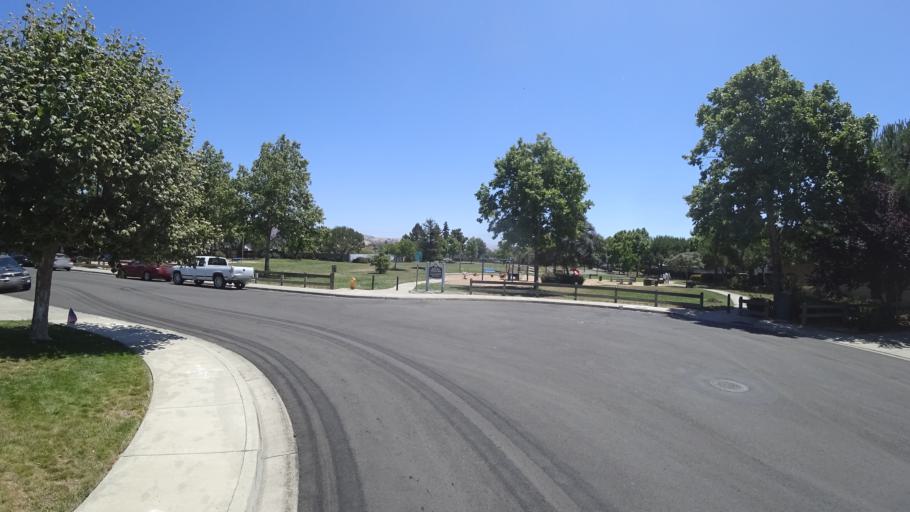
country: US
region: California
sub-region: Alameda County
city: Union City
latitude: 37.6237
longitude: -122.0573
